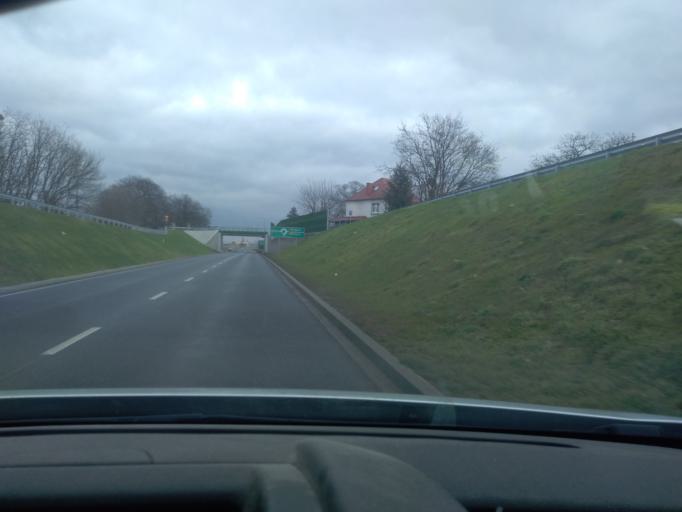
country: PL
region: Greater Poland Voivodeship
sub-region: Powiat obornicki
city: Oborniki
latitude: 52.6545
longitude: 16.8179
